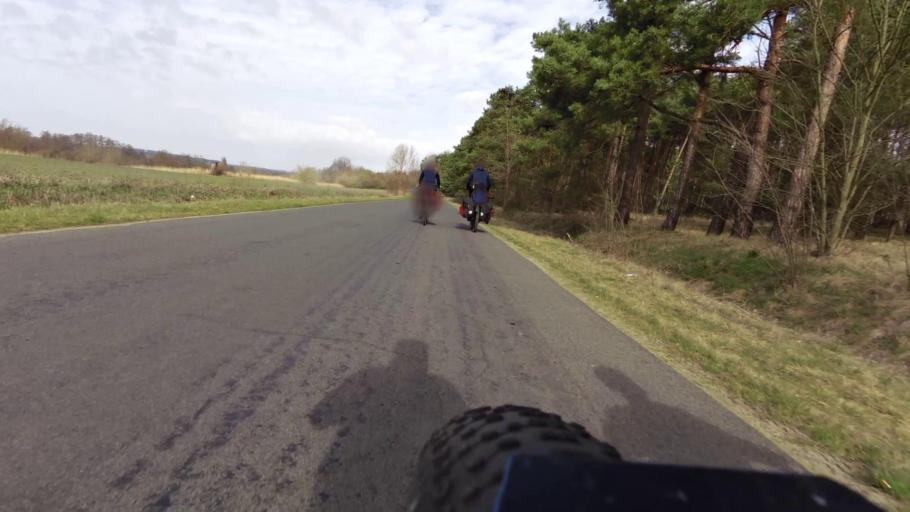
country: DE
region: Brandenburg
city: Brieskow-Finkenheerd
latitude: 52.2902
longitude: 14.6103
